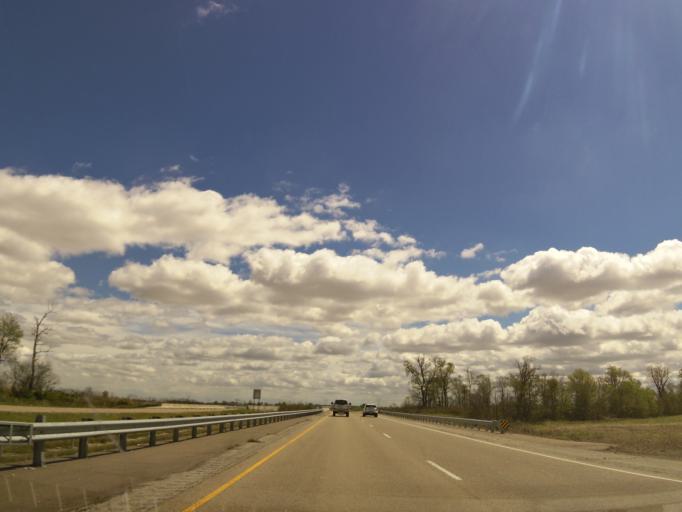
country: US
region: Arkansas
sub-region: Craighead County
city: Bay
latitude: 35.7800
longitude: -90.5938
